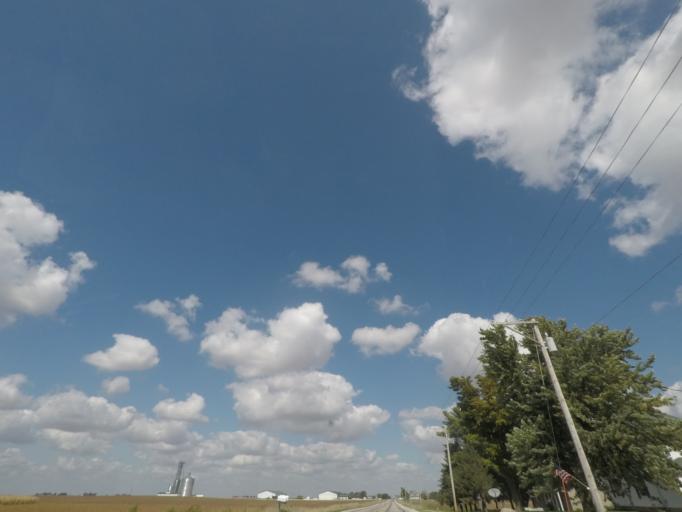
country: US
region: Iowa
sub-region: Story County
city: Nevada
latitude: 42.0444
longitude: -93.4060
